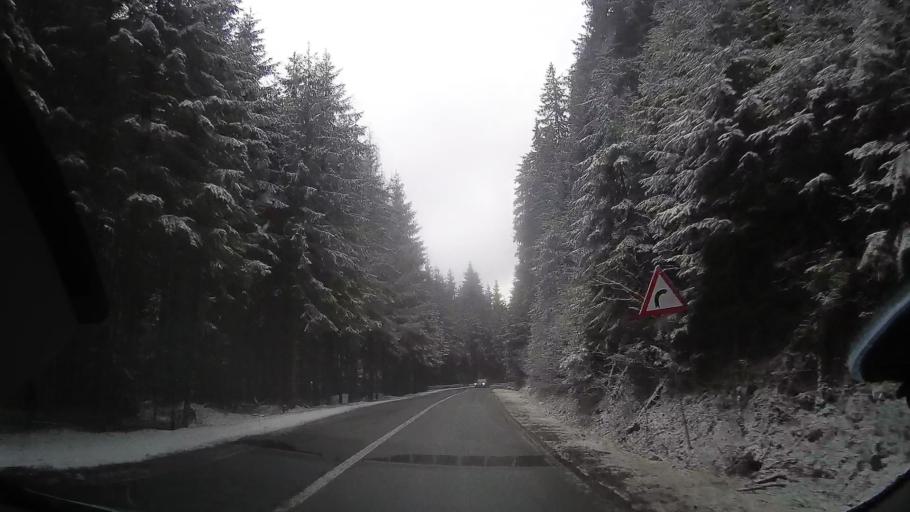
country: RO
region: Cluj
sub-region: Comuna Belis
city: Belis
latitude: 46.6534
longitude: 23.0526
